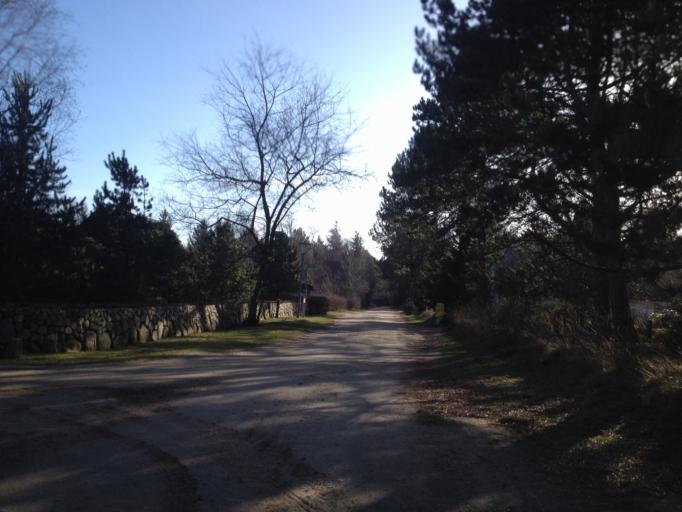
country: DE
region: Schleswig-Holstein
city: Nebel
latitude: 54.6431
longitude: 8.3481
